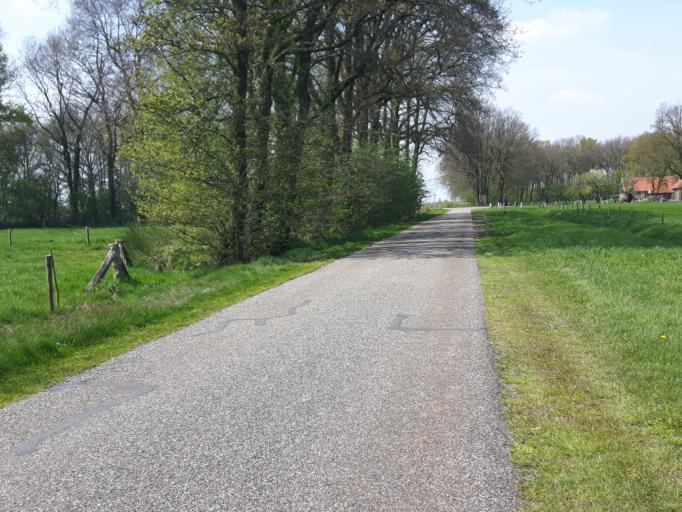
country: NL
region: Overijssel
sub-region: Gemeente Haaksbergen
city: Haaksbergen
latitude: 52.1236
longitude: 6.7965
